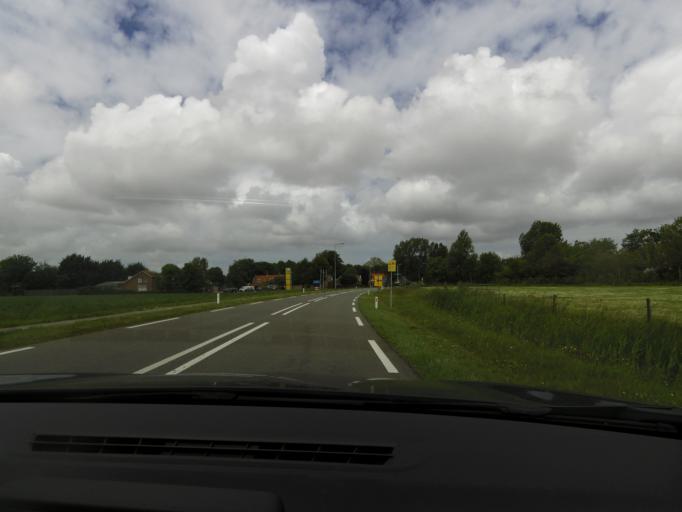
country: NL
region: Zeeland
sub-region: Schouwen-Duiveland
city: Scharendijke
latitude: 51.6918
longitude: 3.9354
